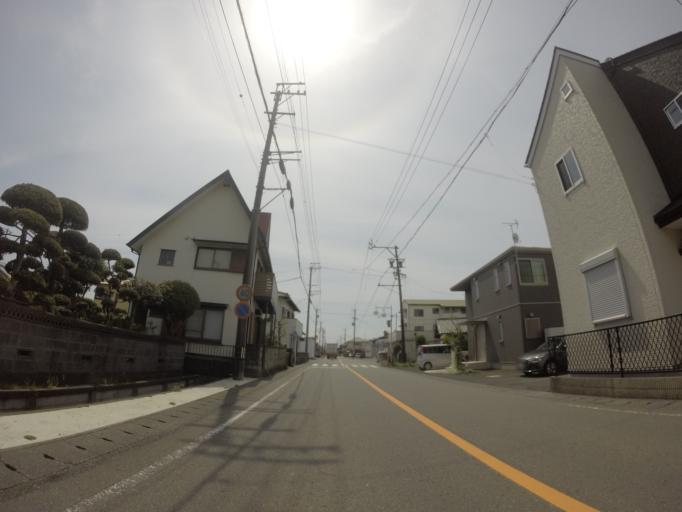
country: JP
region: Shizuoka
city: Fujieda
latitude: 34.8132
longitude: 138.2815
